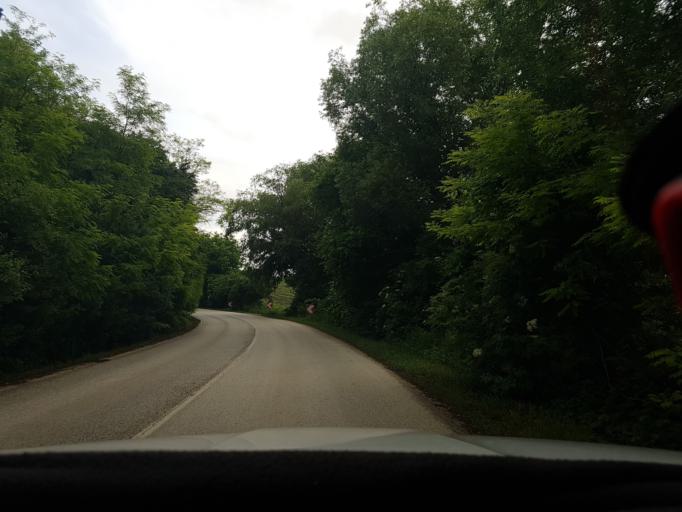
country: HU
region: Pest
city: Perbal
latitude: 47.6278
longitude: 18.7604
